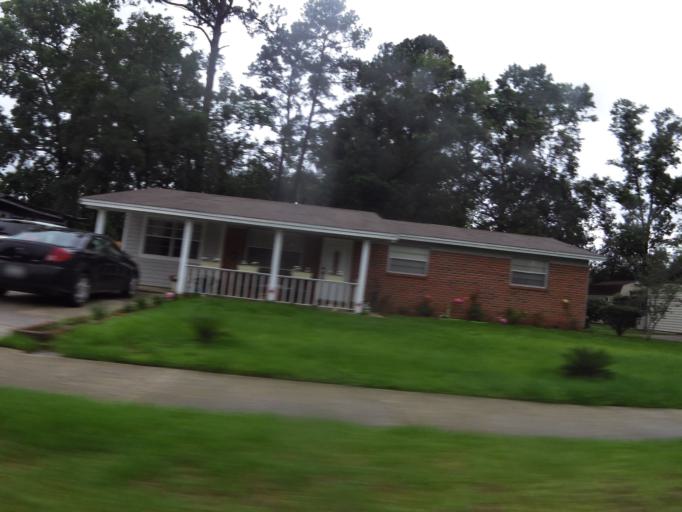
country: US
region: Florida
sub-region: Duval County
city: Jacksonville
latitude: 30.2817
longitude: -81.6255
